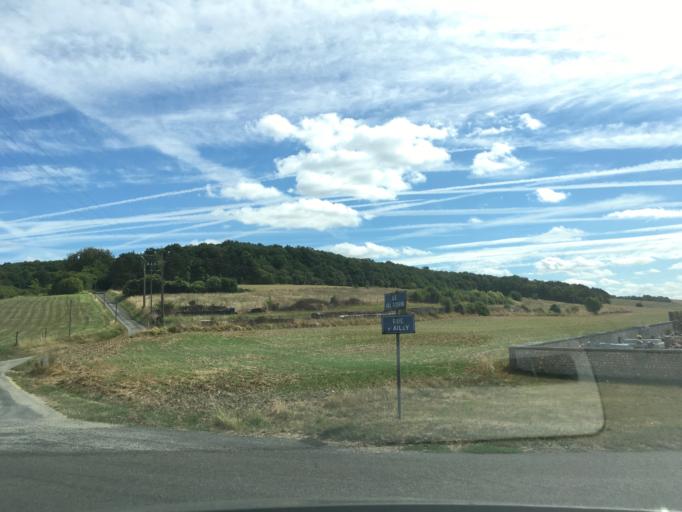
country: FR
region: Haute-Normandie
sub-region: Departement de l'Eure
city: Heudreville-sur-Eure
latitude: 49.1300
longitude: 1.2161
